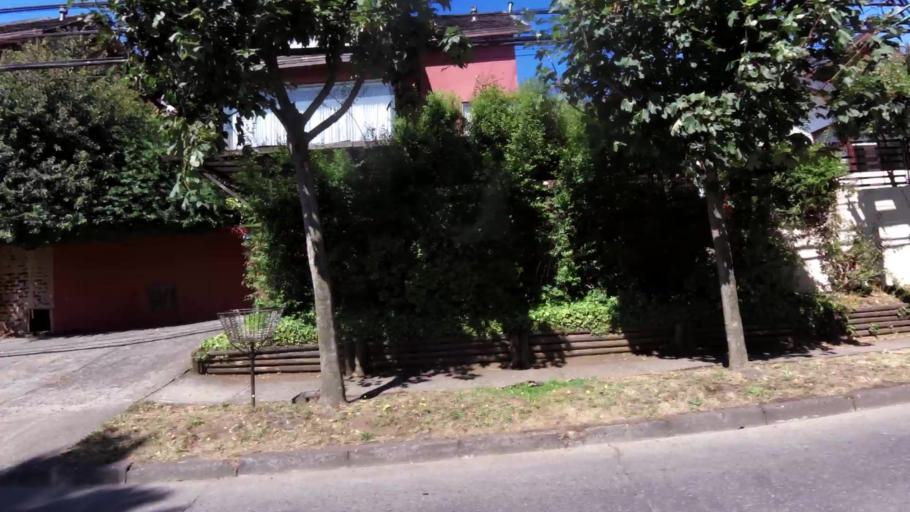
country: CL
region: Biobio
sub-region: Provincia de Concepcion
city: Concepcion
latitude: -36.7935
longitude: -73.0558
